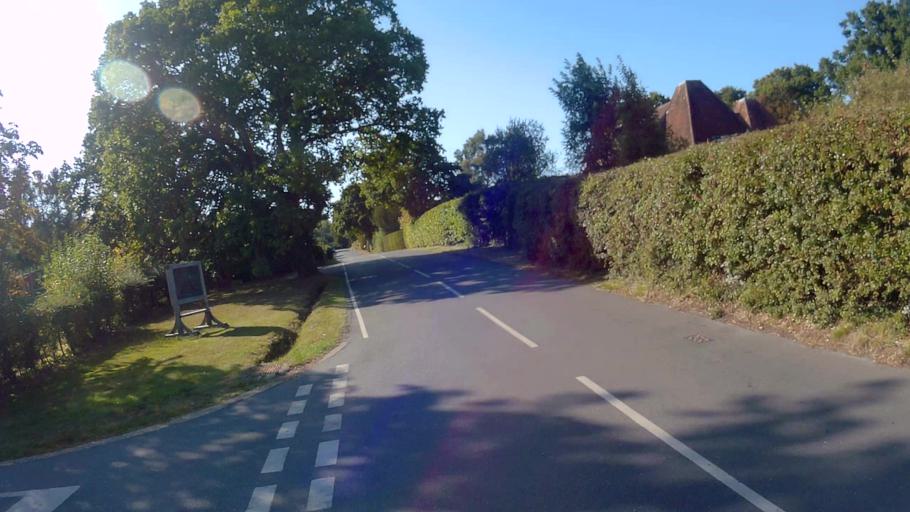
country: GB
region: England
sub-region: Hampshire
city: Lindford
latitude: 51.1588
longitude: -0.8211
